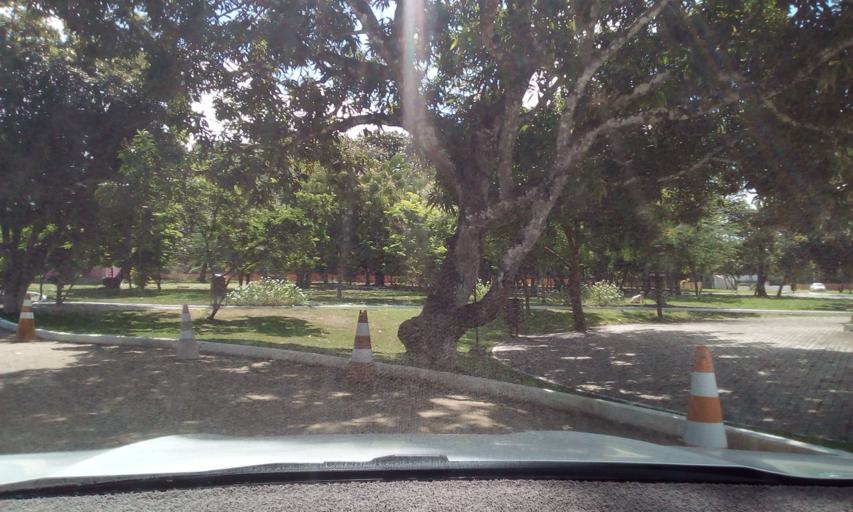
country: BR
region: Paraiba
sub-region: Conde
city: Conde
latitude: -7.2242
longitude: -34.9174
